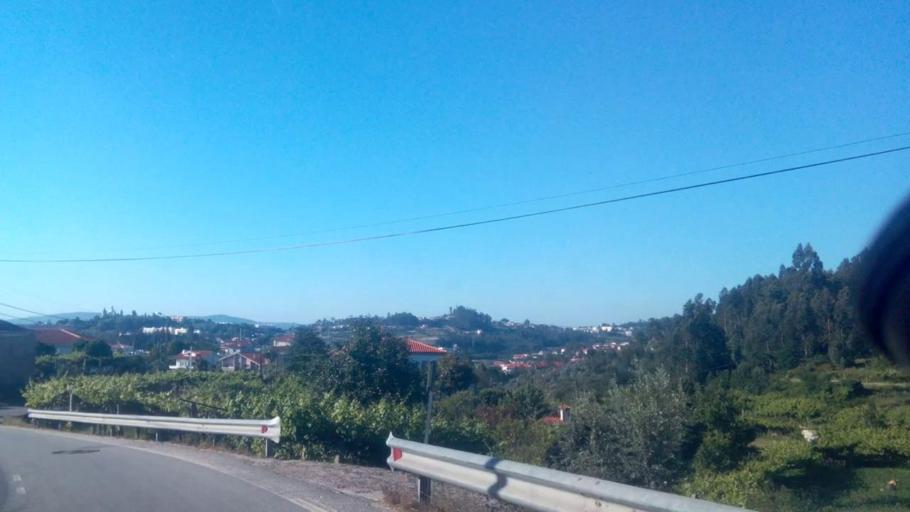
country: PT
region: Porto
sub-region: Penafiel
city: Penafiel
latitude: 41.1921
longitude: -8.2733
